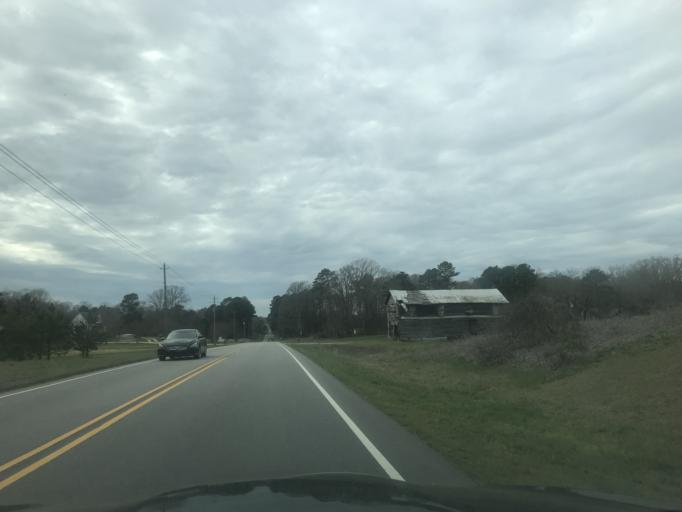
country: US
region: North Carolina
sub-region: Franklin County
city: Franklinton
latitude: 36.0873
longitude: -78.3828
